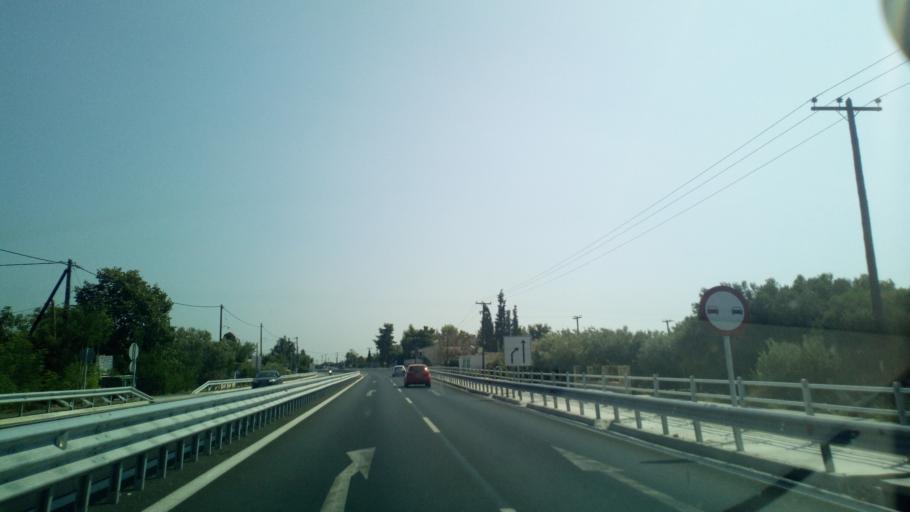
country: GR
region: Central Macedonia
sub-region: Nomos Chalkidikis
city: Nea Potidhaia
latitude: 40.2119
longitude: 23.3219
